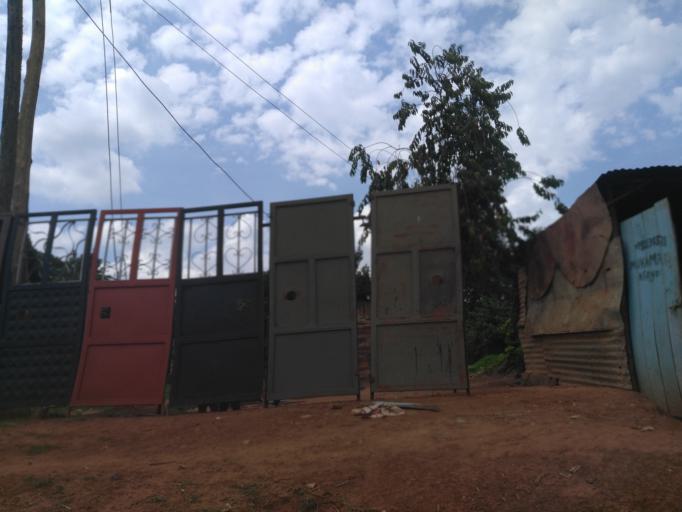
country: UG
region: Central Region
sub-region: Wakiso District
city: Bweyogerere
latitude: 0.4653
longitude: 32.6245
